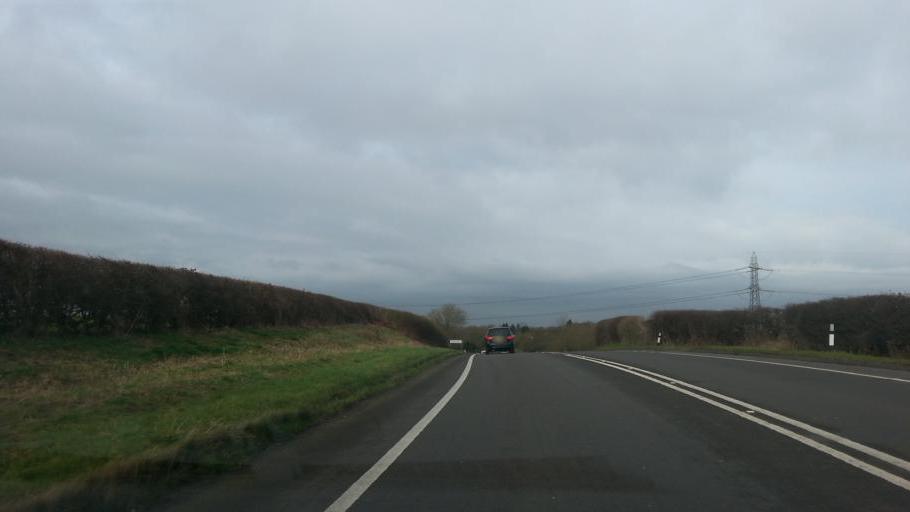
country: GB
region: England
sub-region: Nottinghamshire
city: Cotgrave
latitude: 52.8846
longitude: -1.0693
